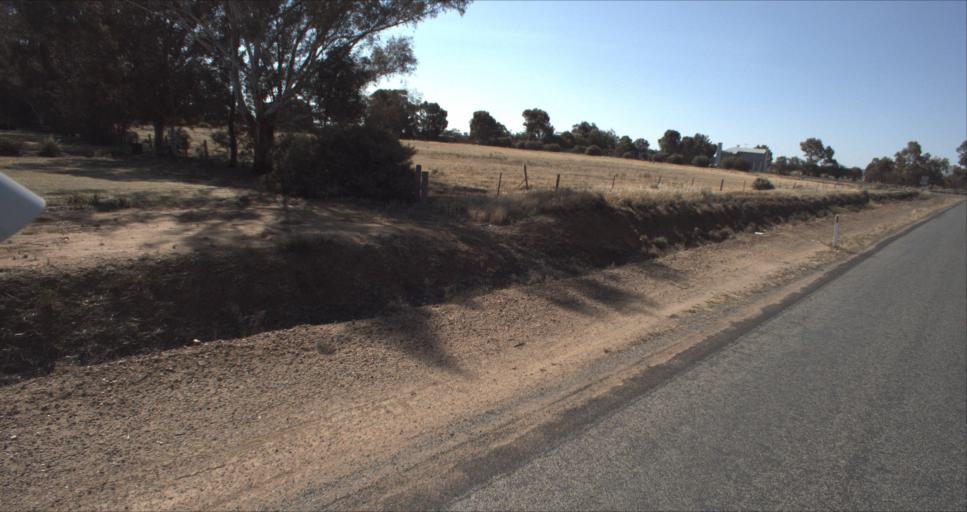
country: AU
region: New South Wales
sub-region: Leeton
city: Leeton
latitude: -34.5371
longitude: 146.4198
